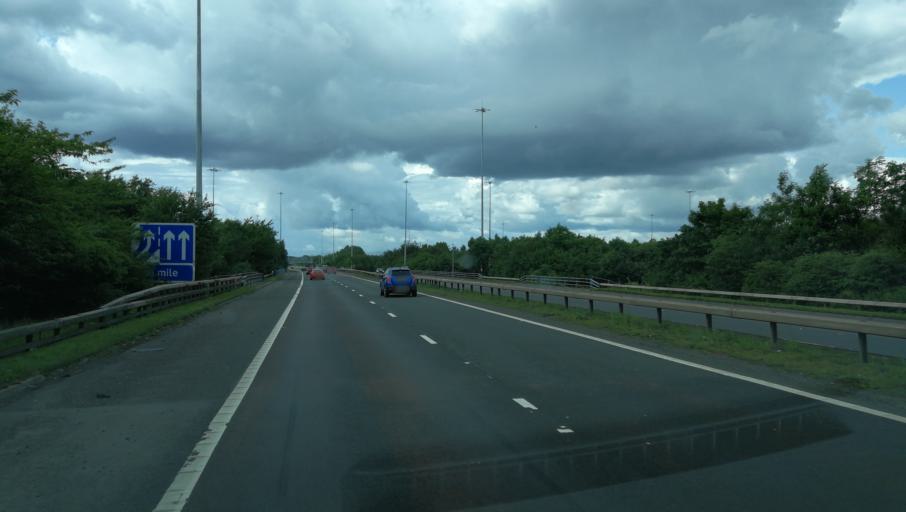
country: GB
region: Scotland
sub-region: South Lanarkshire
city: Hamilton
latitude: 55.7784
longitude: -4.0185
